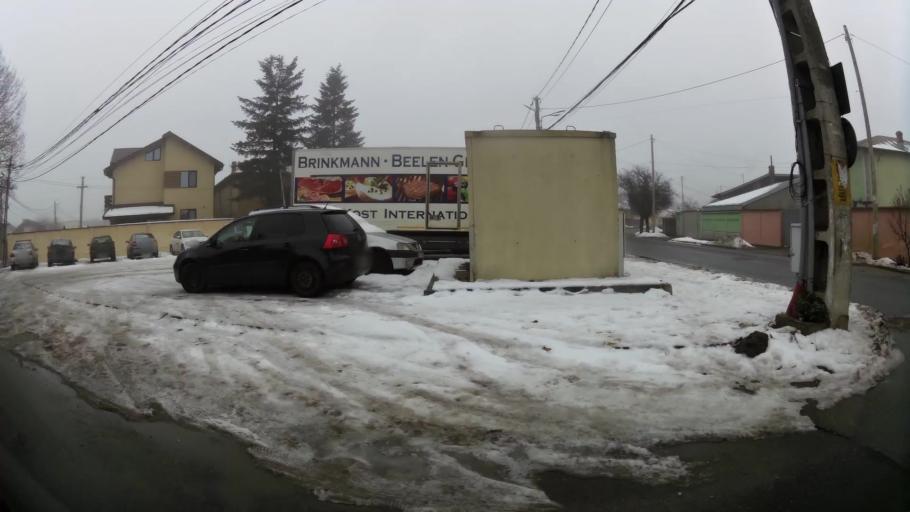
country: RO
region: Ilfov
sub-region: Comuna Chiajna
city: Chiajna
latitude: 44.4571
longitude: 25.9735
